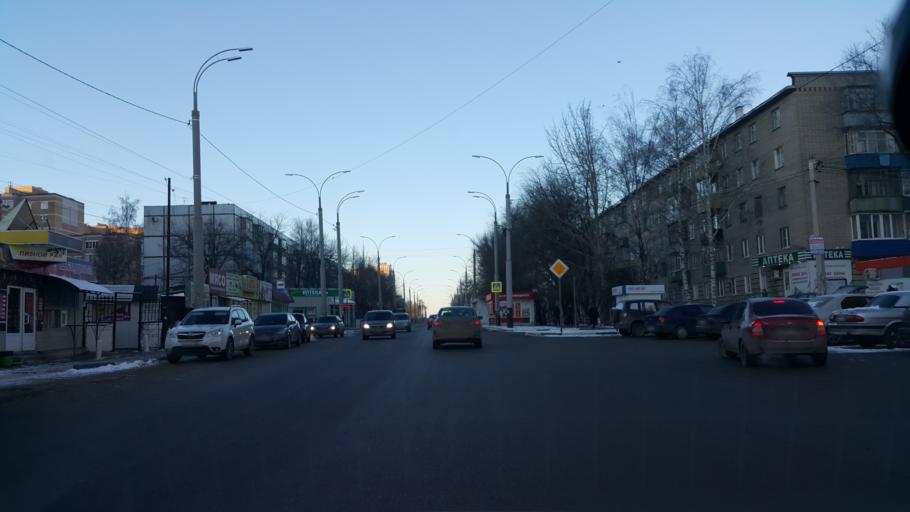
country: RU
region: Tambov
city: Pokrovo-Prigorodnoye
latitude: 52.7046
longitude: 41.3994
